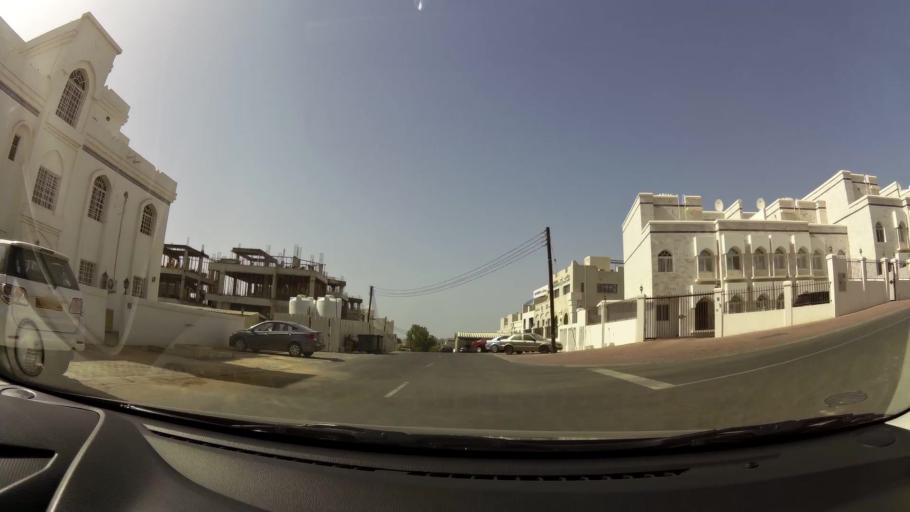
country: OM
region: Muhafazat Masqat
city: Muscat
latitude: 23.6050
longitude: 58.4950
